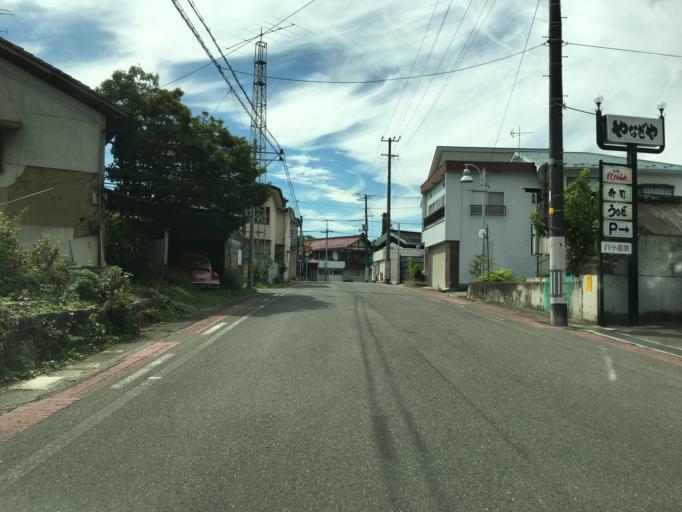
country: JP
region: Fukushima
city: Fukushima-shi
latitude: 37.6564
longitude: 140.5386
